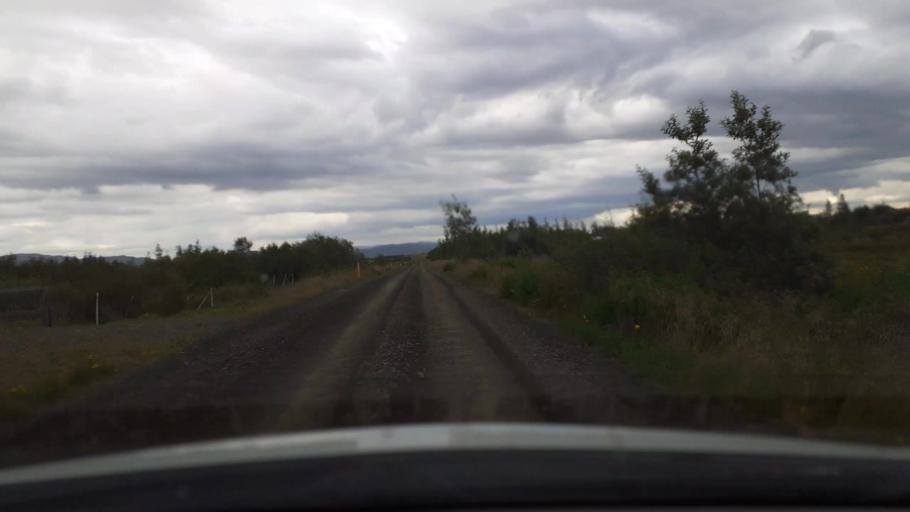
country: IS
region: West
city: Borgarnes
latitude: 64.6249
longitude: -21.9316
